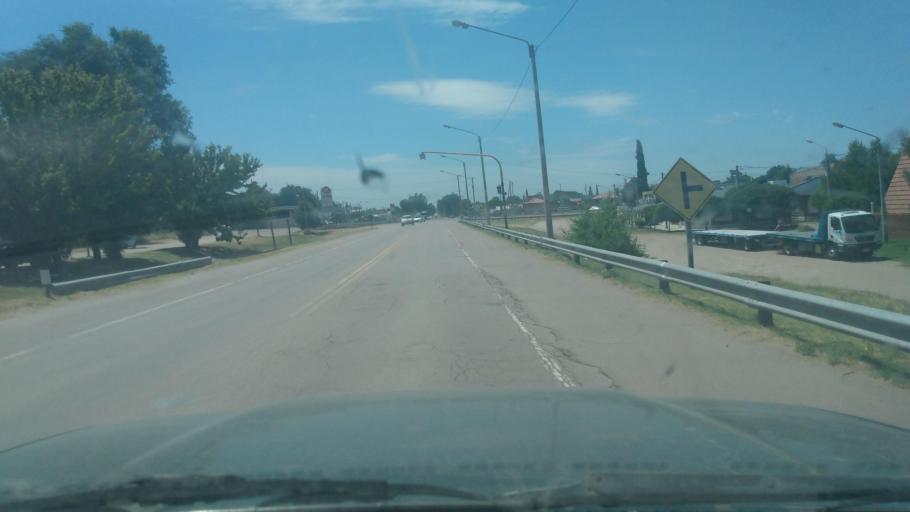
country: AR
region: La Pampa
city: General Acha
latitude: -37.3671
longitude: -64.6027
